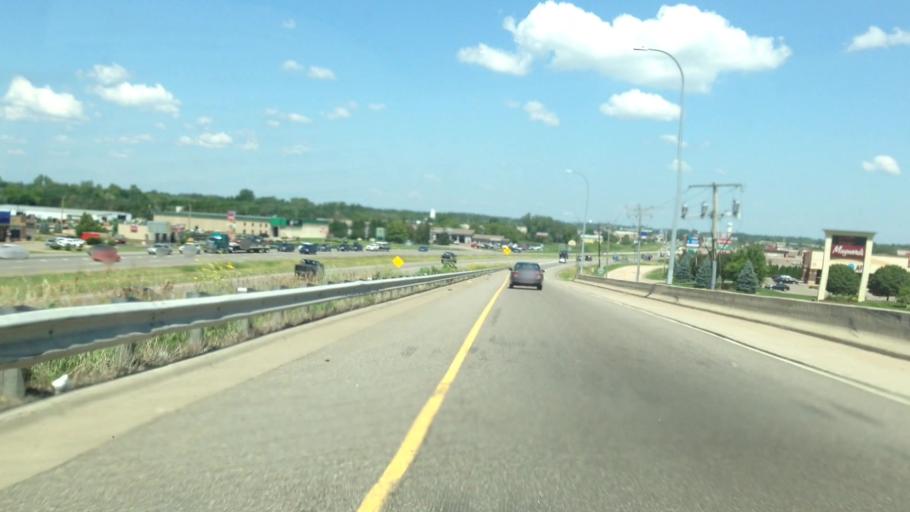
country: US
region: Minnesota
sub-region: Hennepin County
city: Rogers
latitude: 45.2008
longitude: -93.5525
